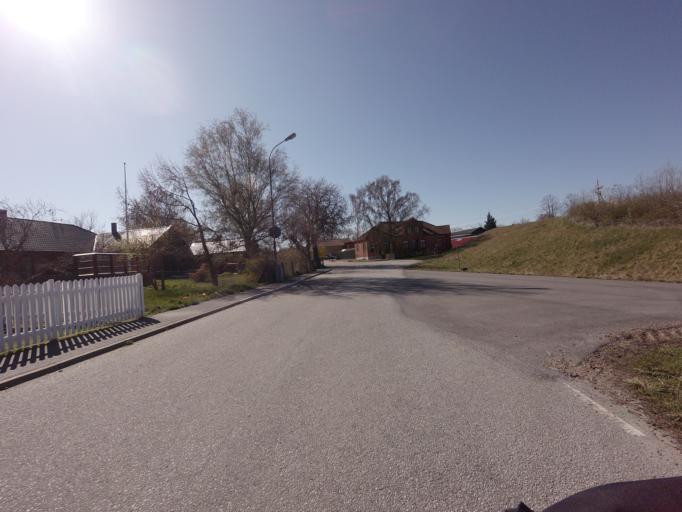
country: SE
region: Skane
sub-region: Malmo
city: Oxie
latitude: 55.4647
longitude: 13.1352
